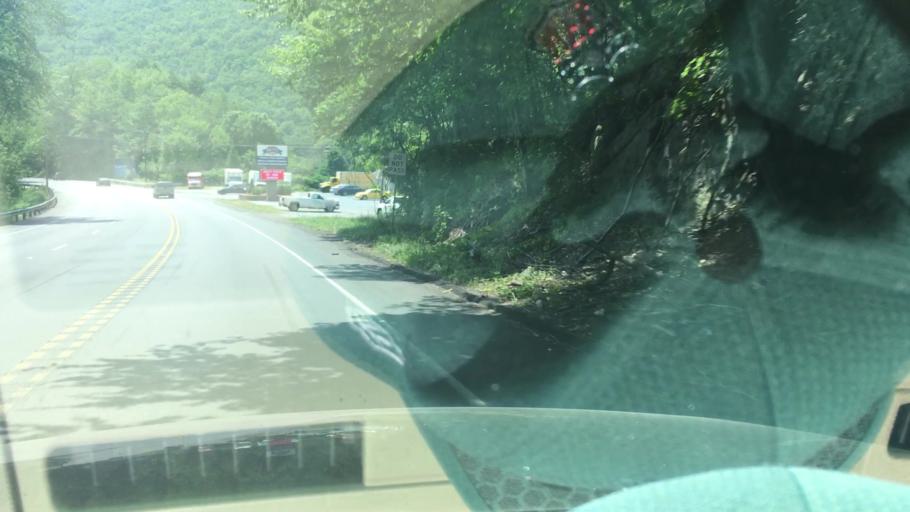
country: US
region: Pennsylvania
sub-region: Schuylkill County
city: Hometown
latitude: 40.8165
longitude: -75.9787
